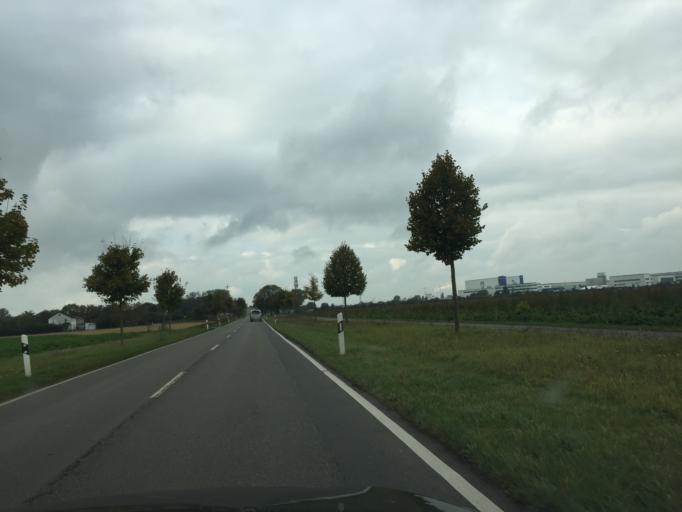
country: DE
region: Baden-Wuerttemberg
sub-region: Karlsruhe Region
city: Eppelheim
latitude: 49.3831
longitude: 8.6449
